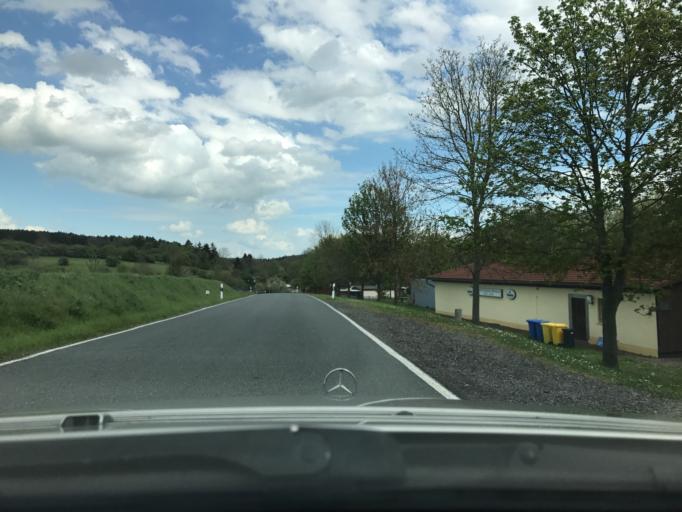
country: DE
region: Thuringia
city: Helmsdorf
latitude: 51.2756
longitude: 10.4134
